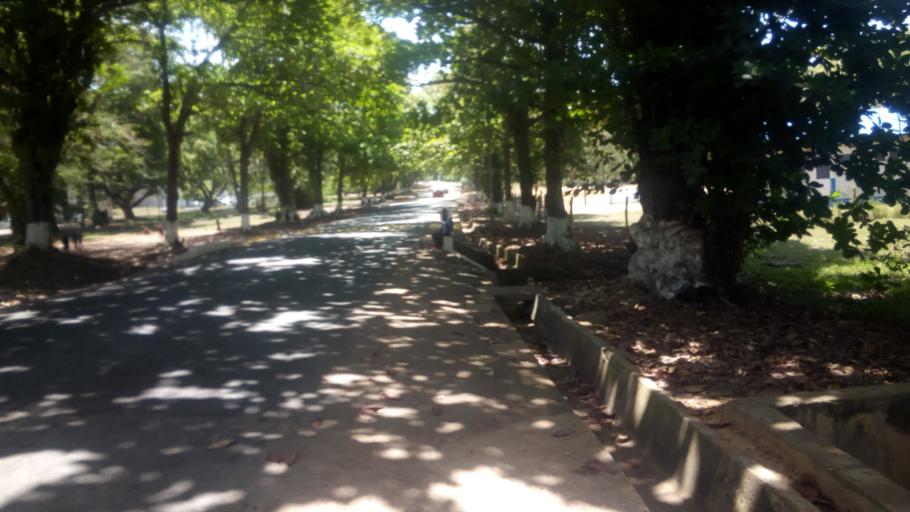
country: GH
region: Central
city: Cape Coast
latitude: 5.1088
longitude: -1.2862
